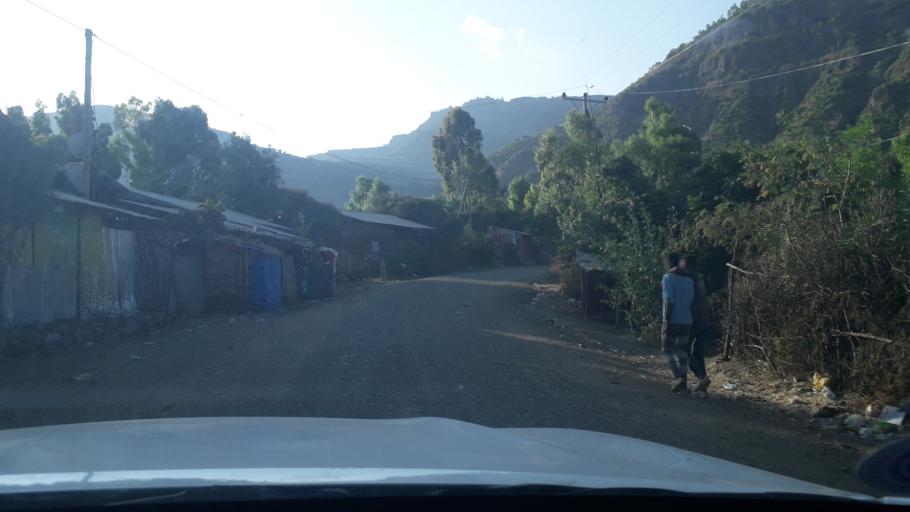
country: ET
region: Amhara
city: Lalibela
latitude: 11.5375
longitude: 39.2455
